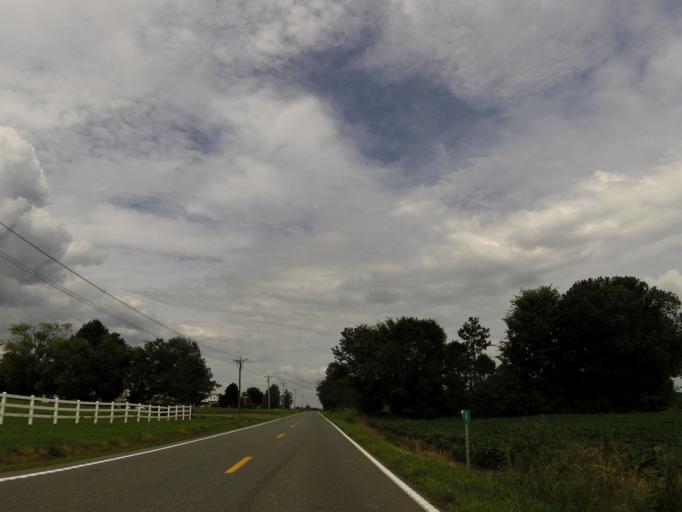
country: US
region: Kentucky
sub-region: McCracken County
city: Massac
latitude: 37.0100
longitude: -88.8215
